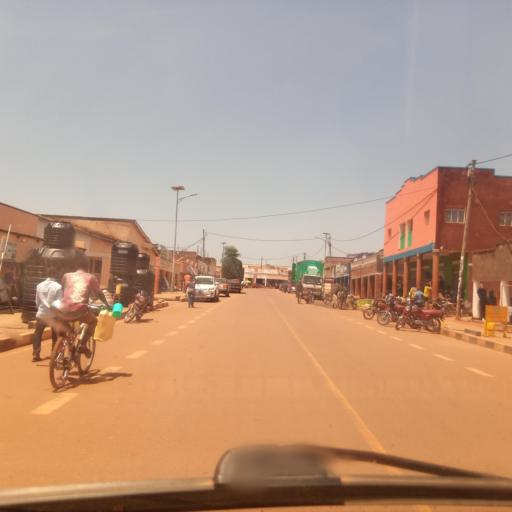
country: UG
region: Northern Region
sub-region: Lira District
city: Lira
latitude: 2.2451
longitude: 32.8950
